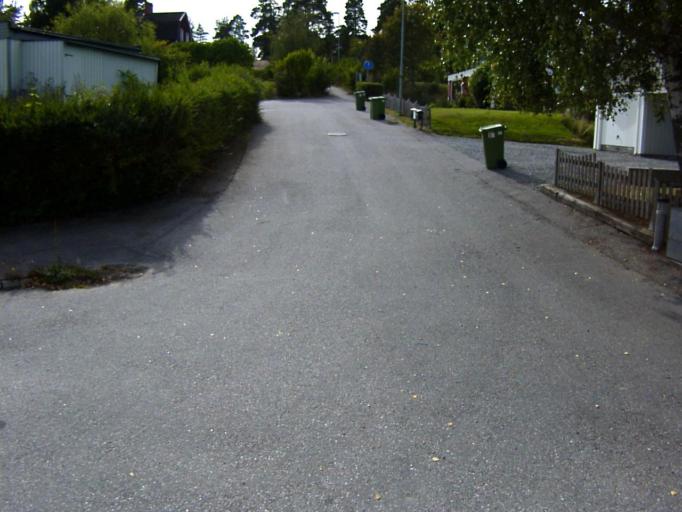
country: SE
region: Soedermanland
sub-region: Eskilstuna Kommun
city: Arla
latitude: 59.3924
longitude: 16.6782
